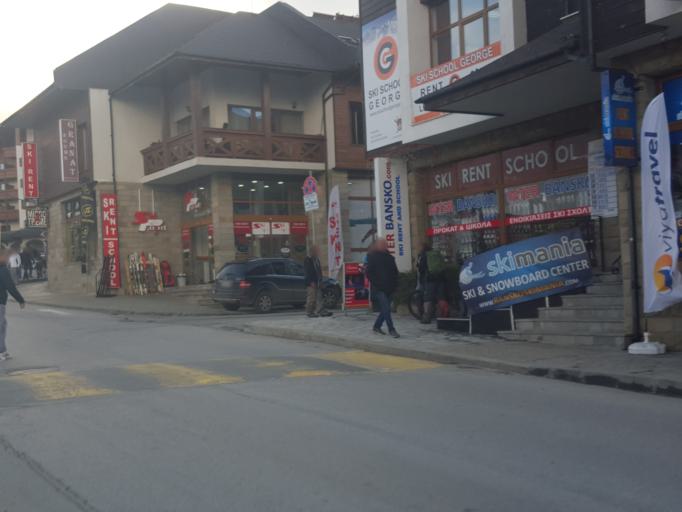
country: BG
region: Blagoevgrad
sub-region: Obshtina Bansko
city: Bansko
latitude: 41.8277
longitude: 23.4793
